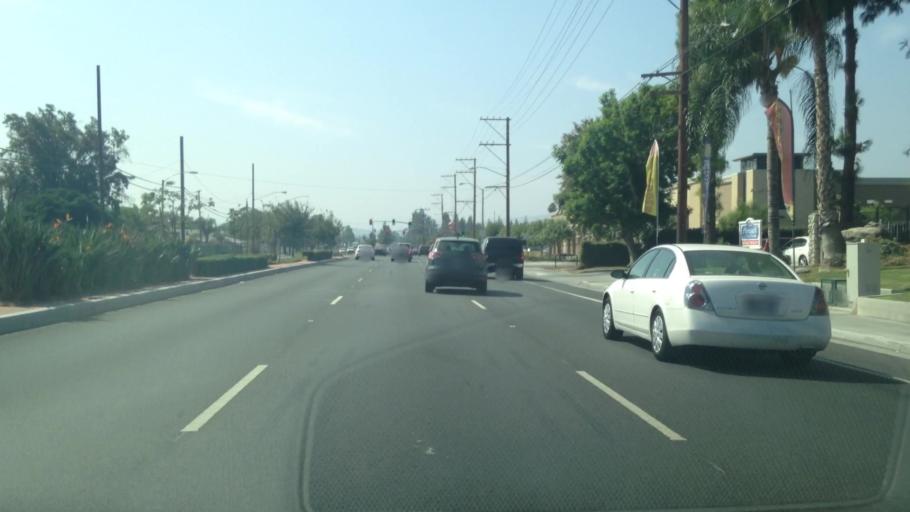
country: US
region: California
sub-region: Riverside County
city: Pedley
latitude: 33.9384
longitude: -117.4541
